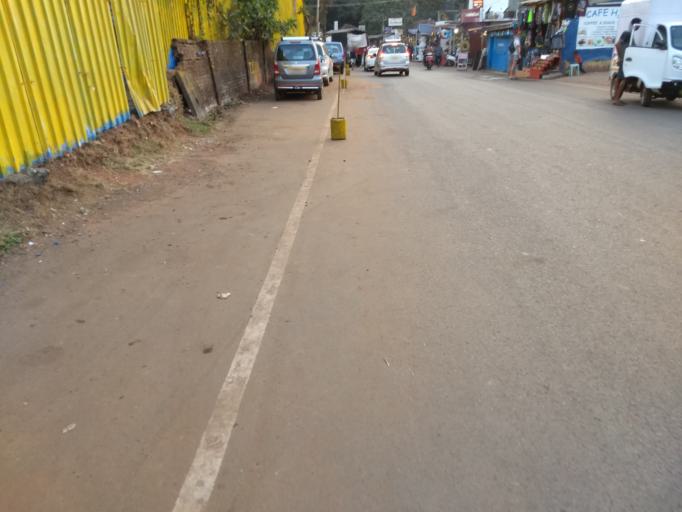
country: IN
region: Goa
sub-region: North Goa
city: Vagator
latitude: 15.5858
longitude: 73.7416
